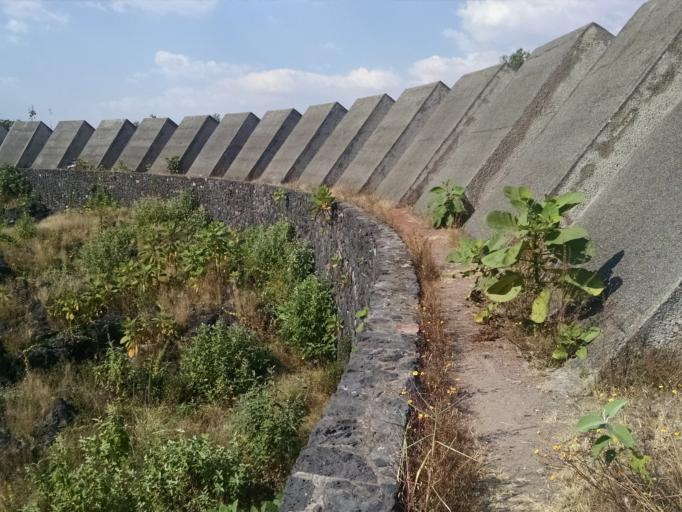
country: MX
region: Mexico City
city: Tlalpan
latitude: 19.3185
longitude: -99.1816
